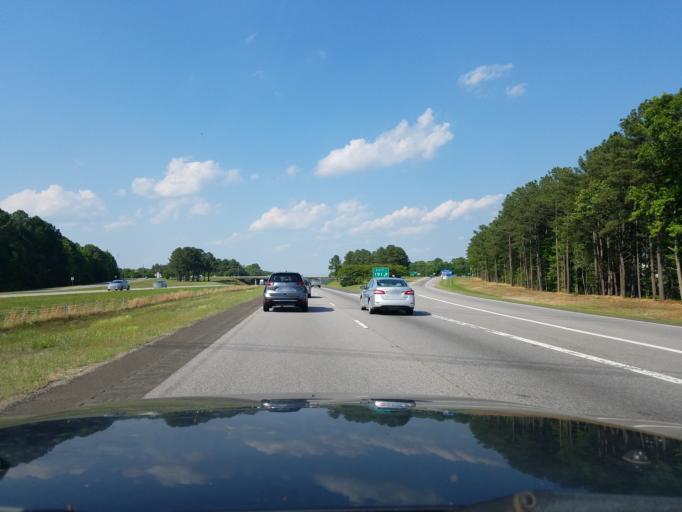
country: US
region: North Carolina
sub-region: Granville County
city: Butner
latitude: 36.1445
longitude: -78.7273
